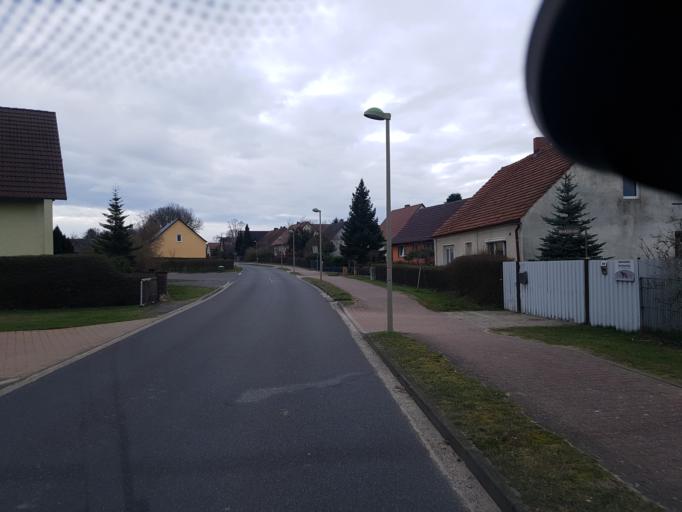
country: DE
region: Brandenburg
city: Gross Lindow
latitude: 52.1464
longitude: 14.5277
